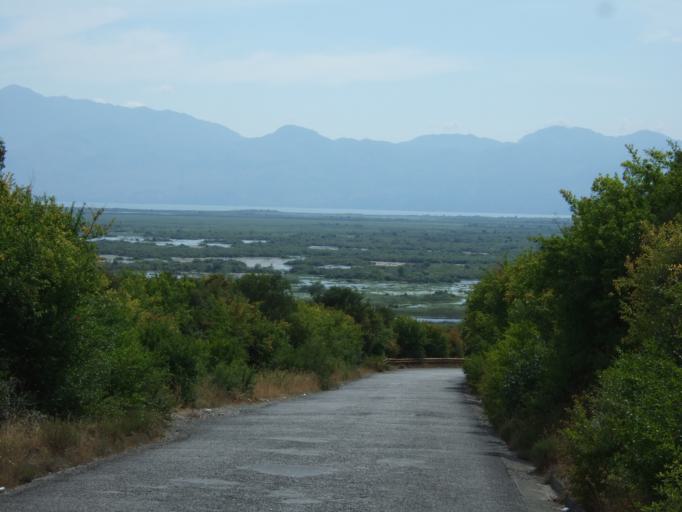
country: ME
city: Tuzi
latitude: 42.3093
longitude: 19.3765
